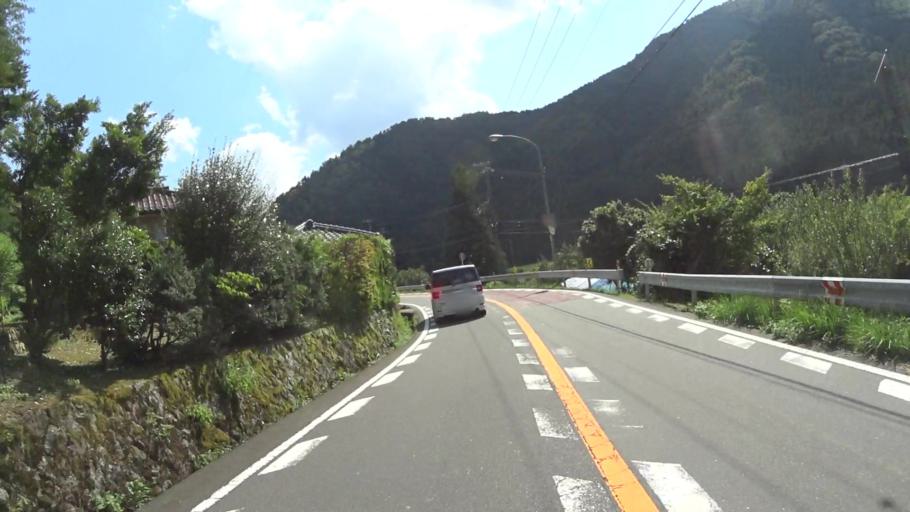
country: JP
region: Kyoto
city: Maizuru
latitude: 35.2997
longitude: 135.5575
